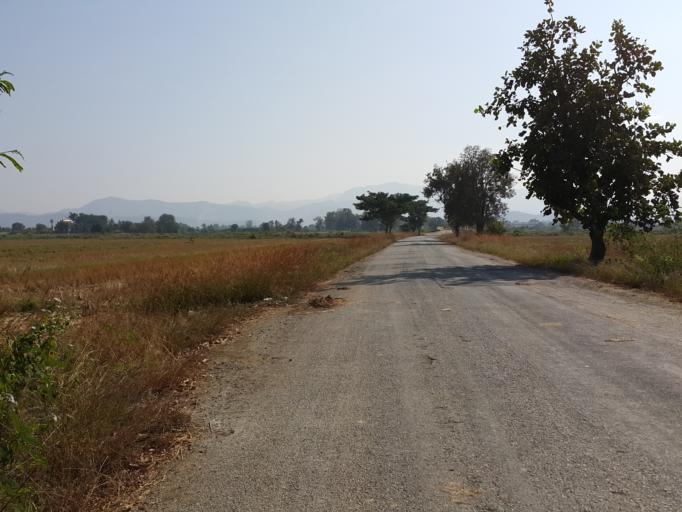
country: TH
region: Chiang Mai
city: San Kamphaeng
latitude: 18.6903
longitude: 99.1249
